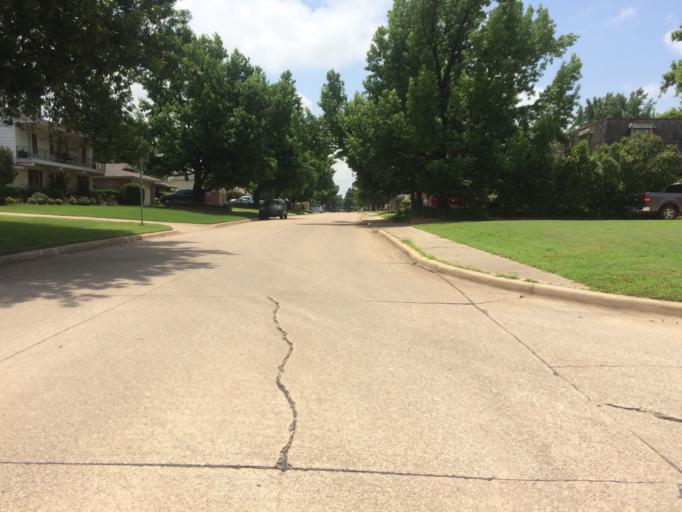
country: US
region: Oklahoma
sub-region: Cleveland County
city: Norman
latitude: 35.2208
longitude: -97.4683
